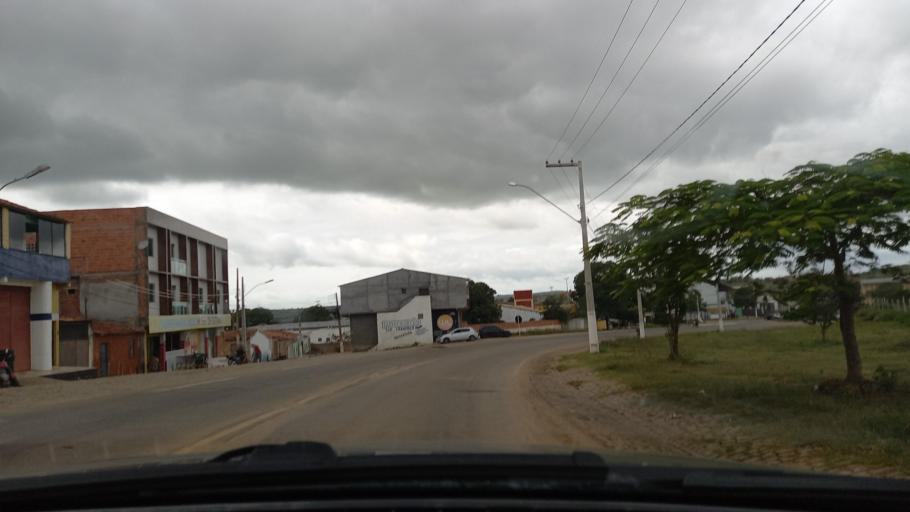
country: BR
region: Sergipe
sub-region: Caninde De Sao Francisco
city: Caninde de Sao Francisco
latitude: -9.6660
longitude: -37.7949
